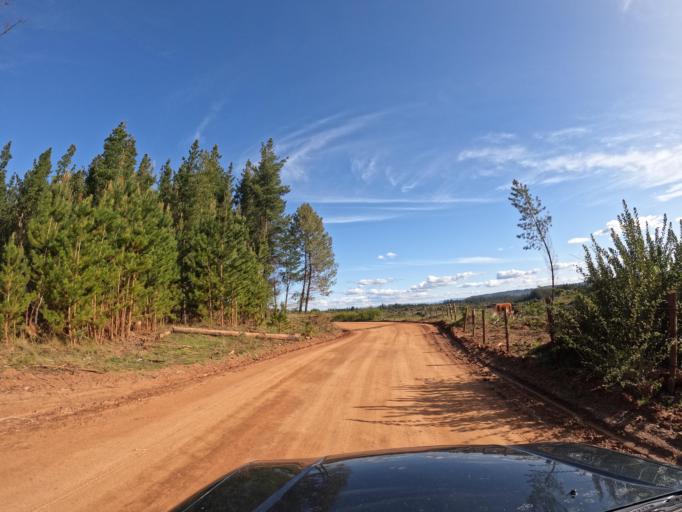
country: CL
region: Biobio
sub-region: Provincia de Biobio
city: La Laja
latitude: -37.1056
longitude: -72.7423
